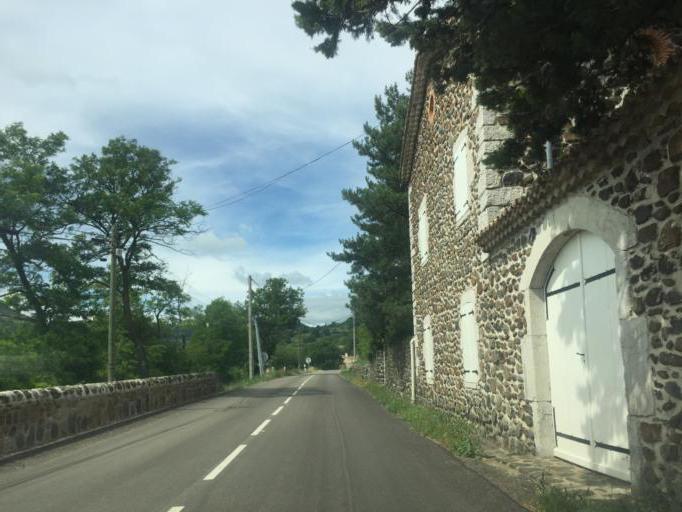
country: FR
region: Rhone-Alpes
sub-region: Departement de l'Ardeche
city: Villeneuve-de-Berg
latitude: 44.5948
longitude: 4.5360
